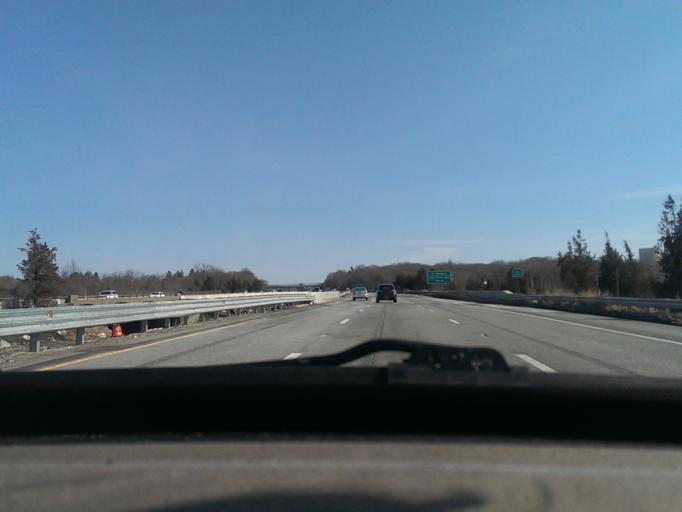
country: US
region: Massachusetts
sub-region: Bristol County
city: Ocean Grove
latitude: 41.7367
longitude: -71.2041
